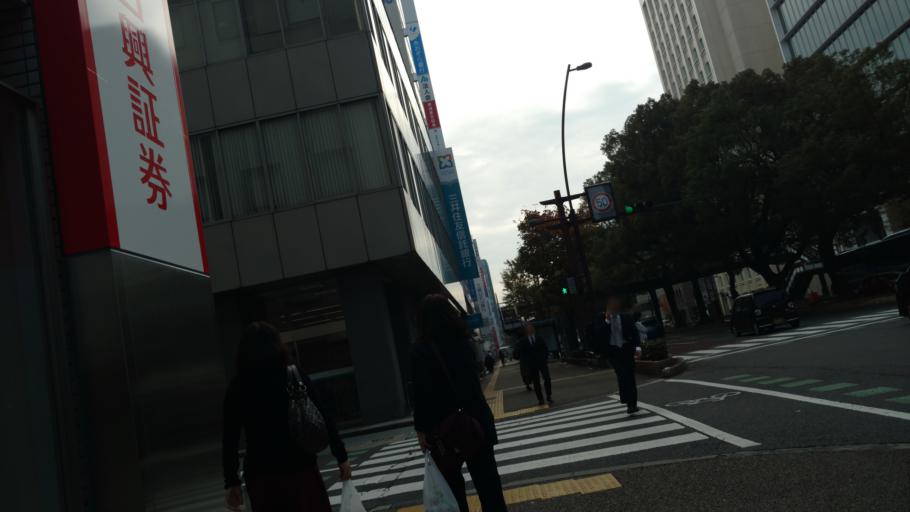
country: JP
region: Kagawa
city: Takamatsu-shi
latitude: 34.3446
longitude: 134.0483
